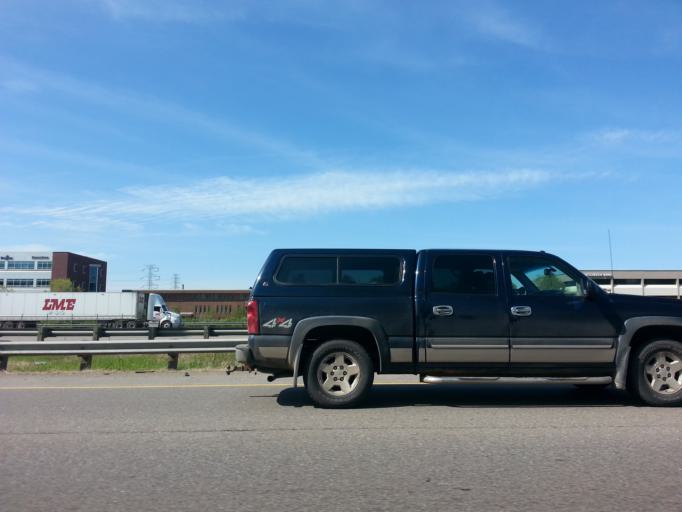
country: US
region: Minnesota
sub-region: Ramsey County
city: Lauderdale
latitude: 45.0100
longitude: -93.1979
